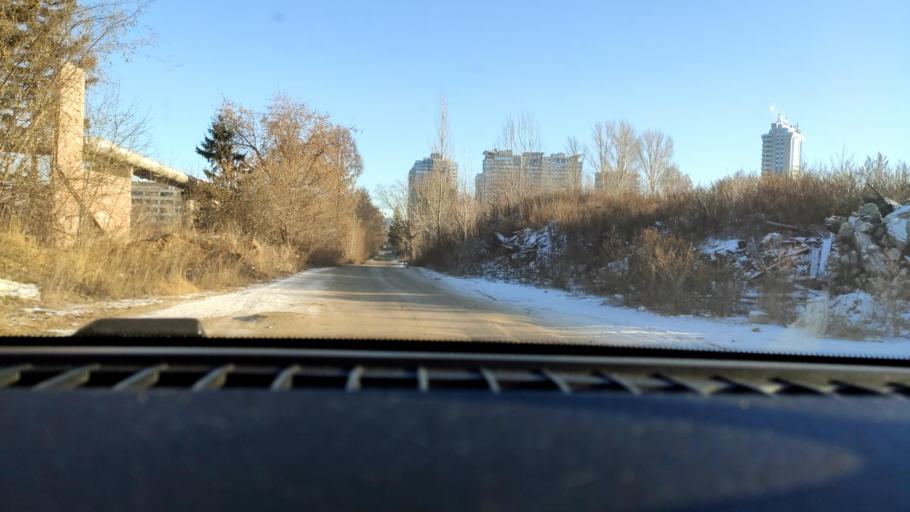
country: RU
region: Samara
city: Samara
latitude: 53.2188
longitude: 50.1452
